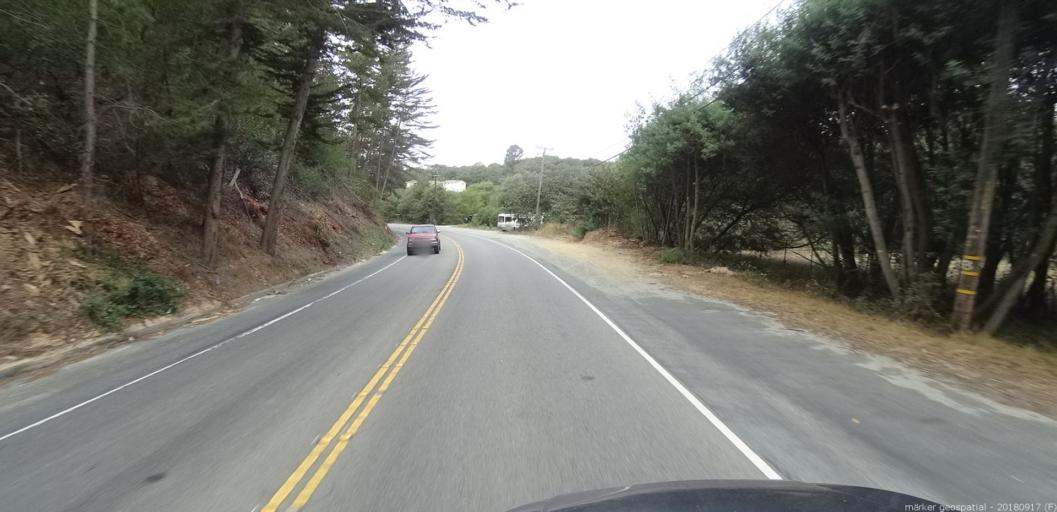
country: US
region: California
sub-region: Monterey County
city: Prunedale
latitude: 36.8000
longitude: -121.6965
